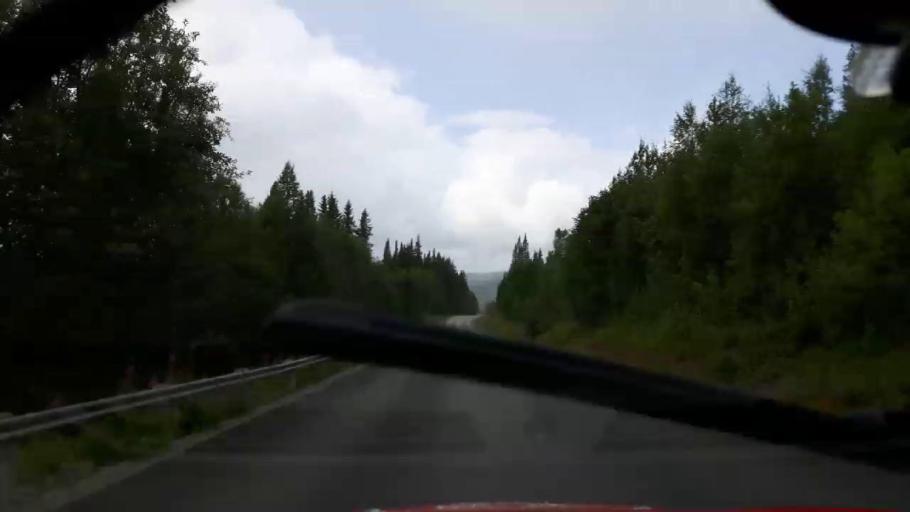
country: SE
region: Vaesterbotten
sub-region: Vilhelmina Kommun
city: Sjoberg
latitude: 64.9431
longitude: 15.7923
